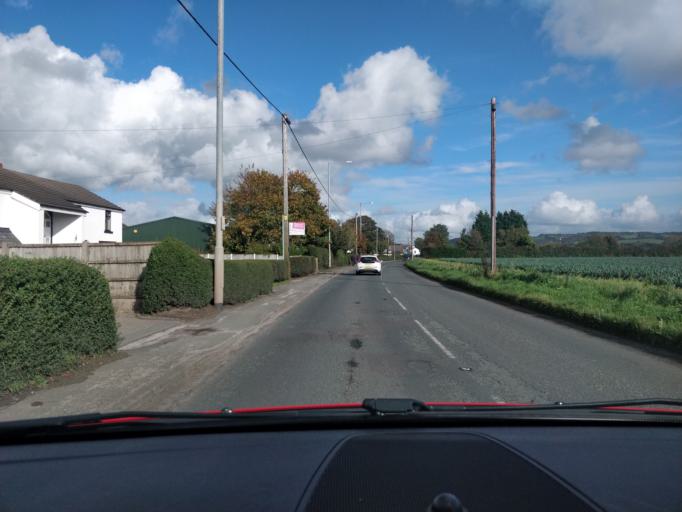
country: GB
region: England
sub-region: Lancashire
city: Parbold
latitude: 53.5966
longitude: -2.8084
